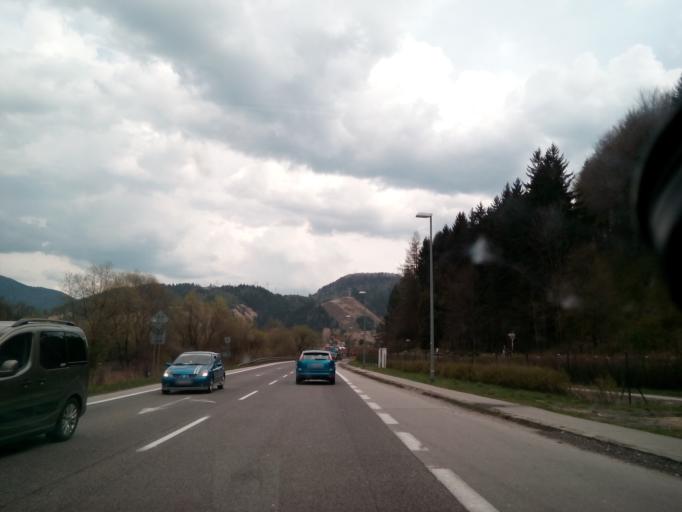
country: SK
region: Zilinsky
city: Ruzomberok
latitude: 49.1199
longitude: 19.1752
